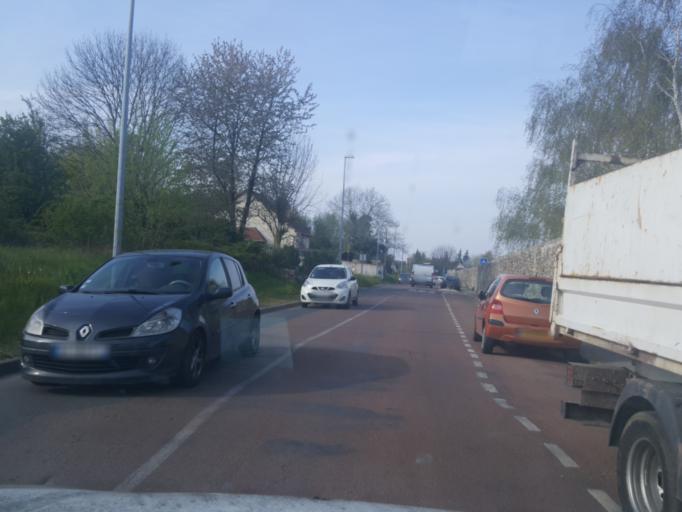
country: FR
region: Ile-de-France
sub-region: Departement de l'Essonne
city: Longpont-sur-Orge
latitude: 48.6381
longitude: 2.2900
